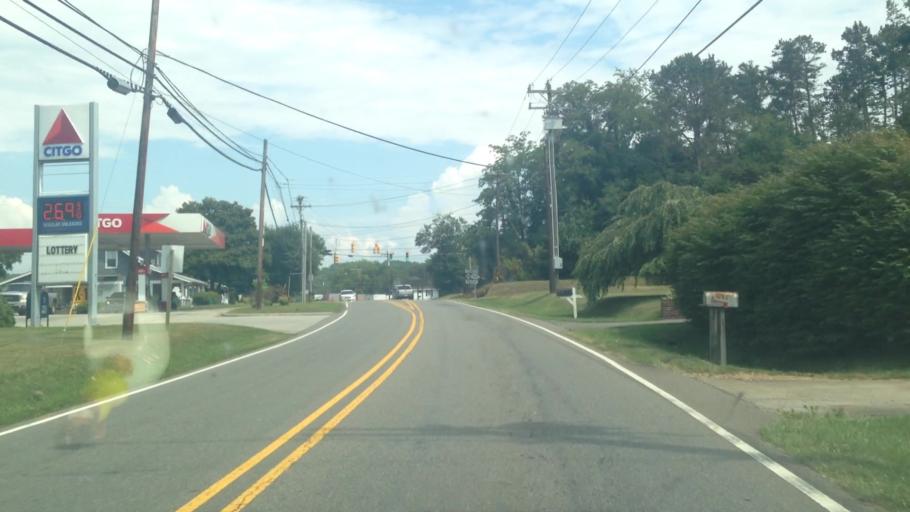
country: US
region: North Carolina
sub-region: Surry County
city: Mount Airy
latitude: 36.4872
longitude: -80.5920
